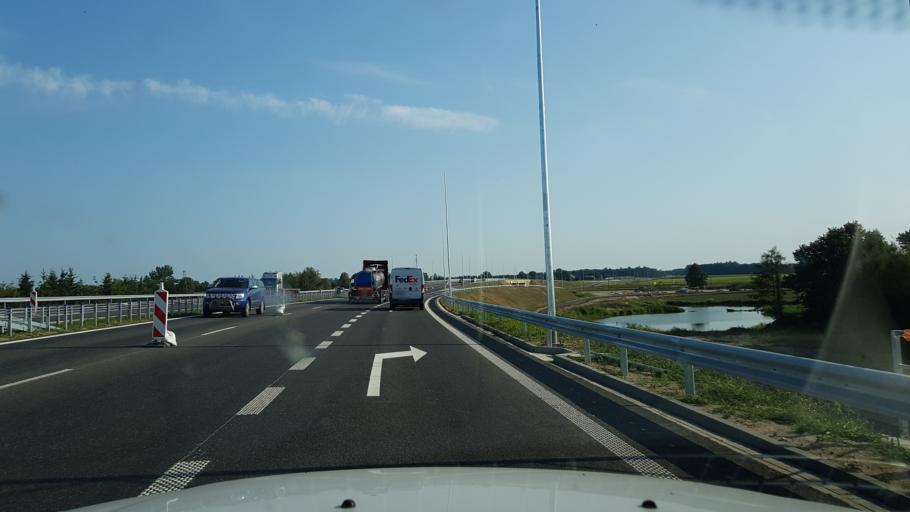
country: PL
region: West Pomeranian Voivodeship
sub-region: Powiat gryficki
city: Ploty
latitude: 53.8155
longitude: 15.2502
